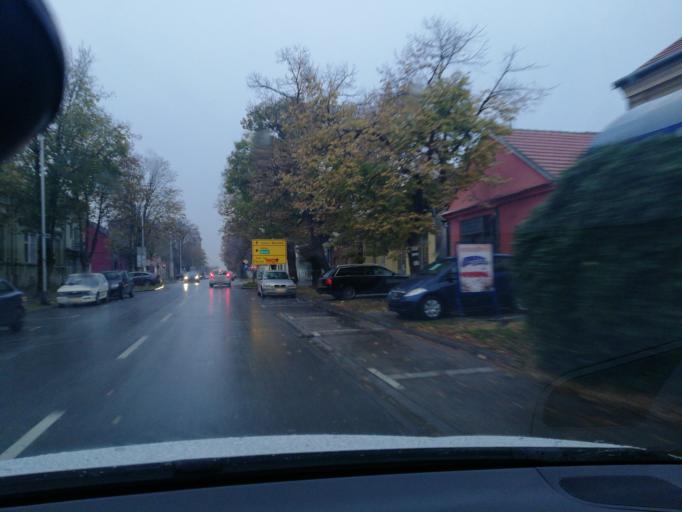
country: RS
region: Autonomna Pokrajina Vojvodina
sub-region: Sremski Okrug
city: Ruma
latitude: 45.0081
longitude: 19.8173
